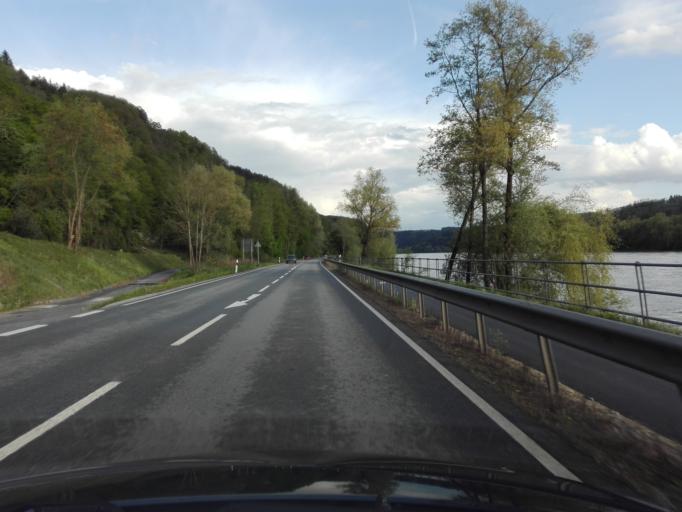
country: DE
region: Bavaria
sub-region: Lower Bavaria
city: Thyrnau
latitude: 48.5876
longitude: 13.5280
